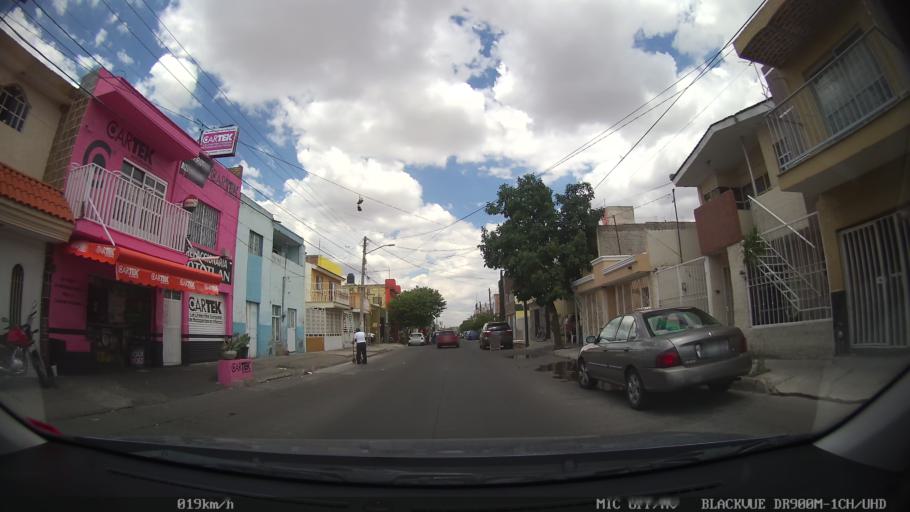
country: MX
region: Jalisco
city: Tlaquepaque
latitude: 20.6507
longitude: -103.2792
